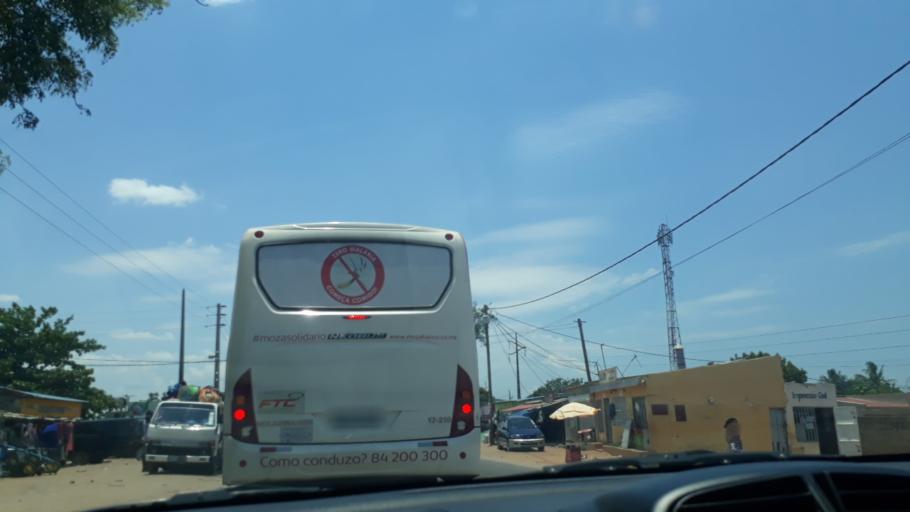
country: MZ
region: Maputo City
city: Maputo
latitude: -25.8925
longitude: 32.6022
